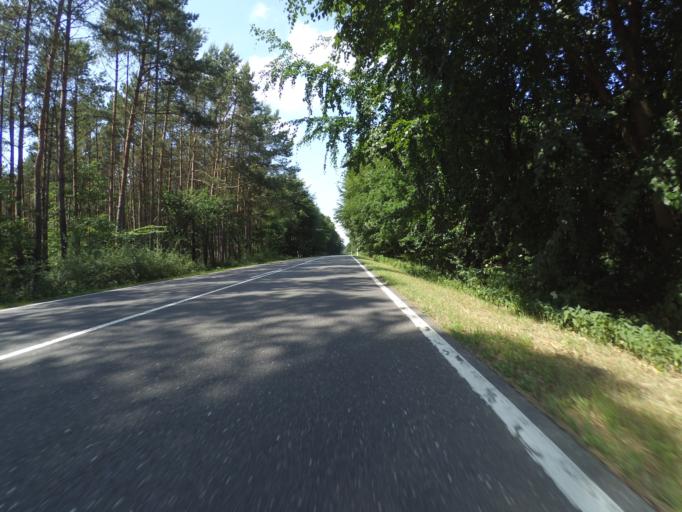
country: DE
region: Mecklenburg-Vorpommern
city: Plau am See
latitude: 53.3943
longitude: 12.2925
